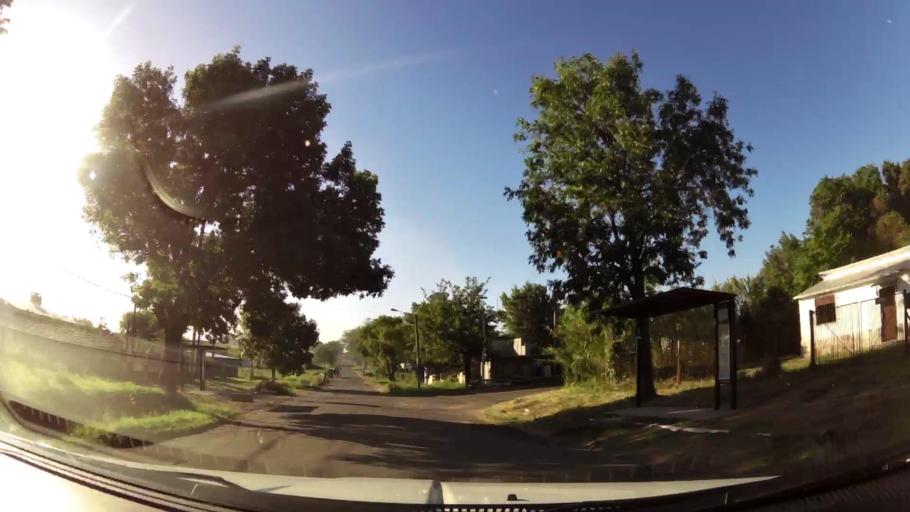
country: UY
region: Canelones
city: La Paz
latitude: -34.8323
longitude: -56.2407
